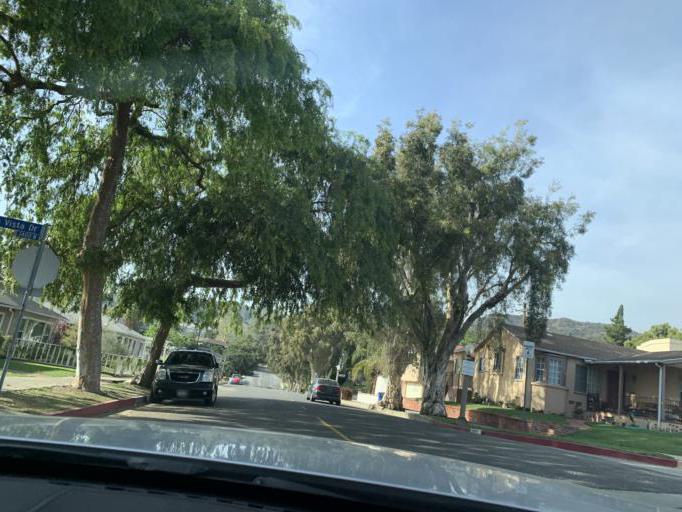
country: US
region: California
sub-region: Los Angeles County
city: Pasadena
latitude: 34.1423
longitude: -118.1925
